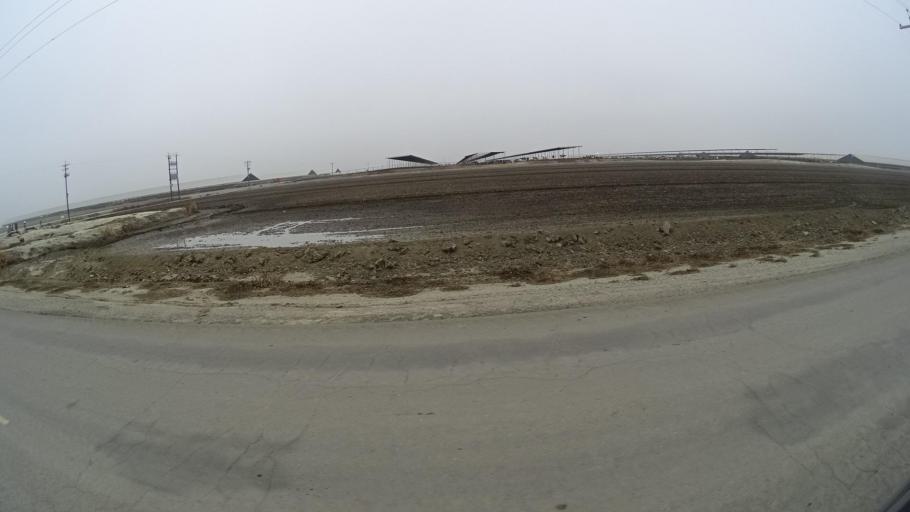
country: US
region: California
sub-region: Kern County
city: Rosedale
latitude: 35.2095
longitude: -119.2077
